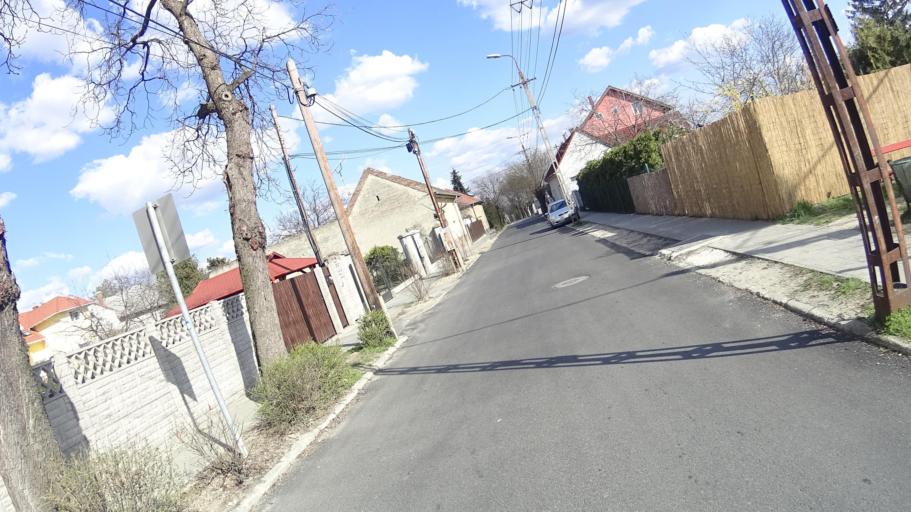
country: HU
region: Budapest
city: Budapest XXII. keruelet
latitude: 47.4261
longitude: 19.0281
